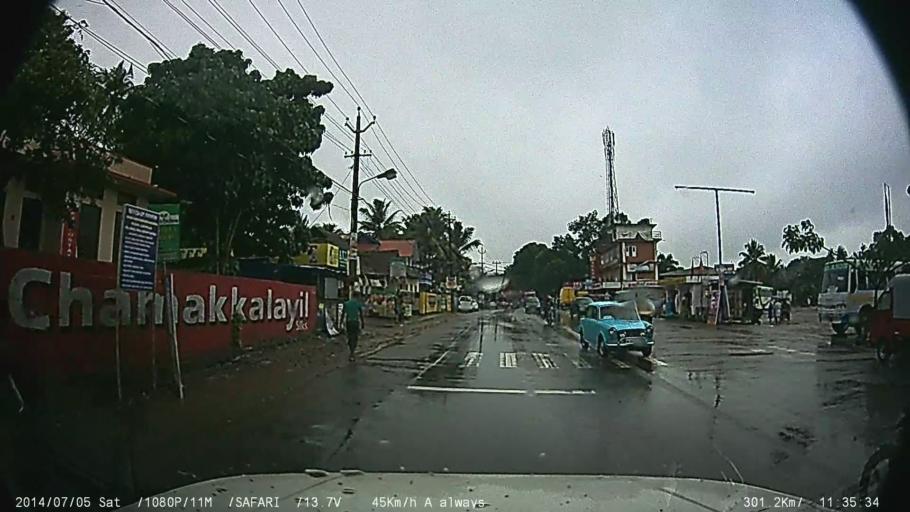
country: IN
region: Kerala
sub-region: Ernakulam
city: Muvattupula
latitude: 9.9792
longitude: 76.5865
